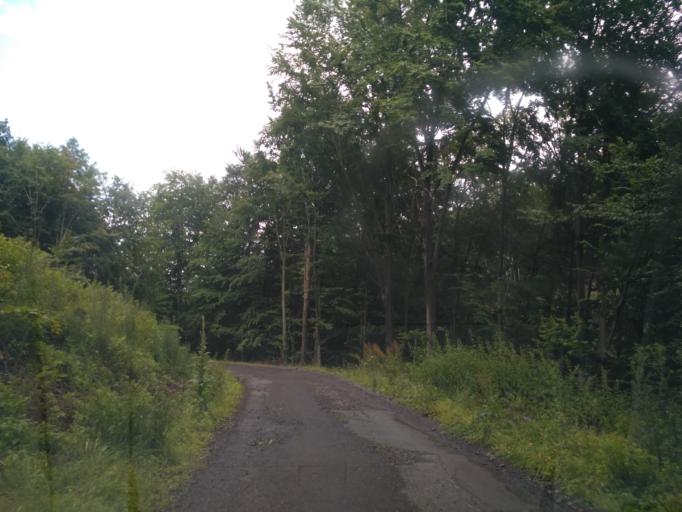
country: SK
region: Kosicky
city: Secovce
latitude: 48.5971
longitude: 21.5091
